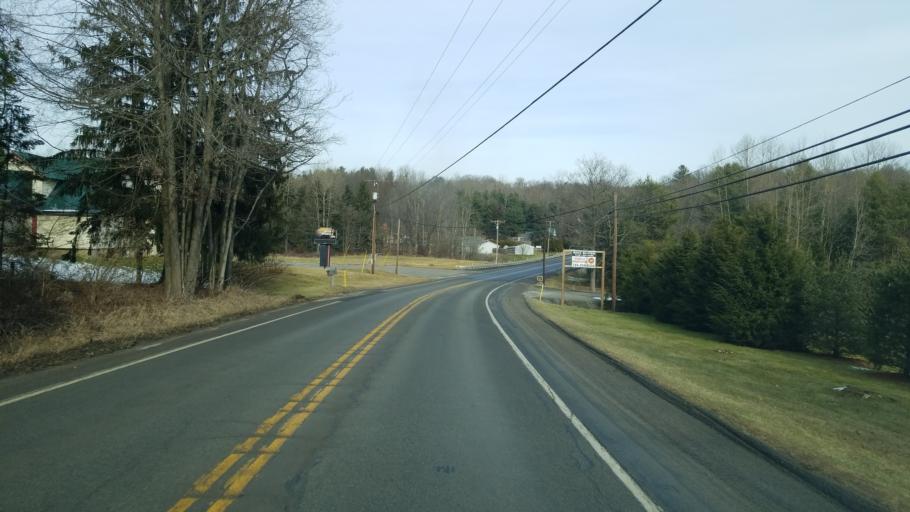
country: US
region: Pennsylvania
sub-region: Indiana County
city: Clymer
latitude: 40.7294
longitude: -78.9361
